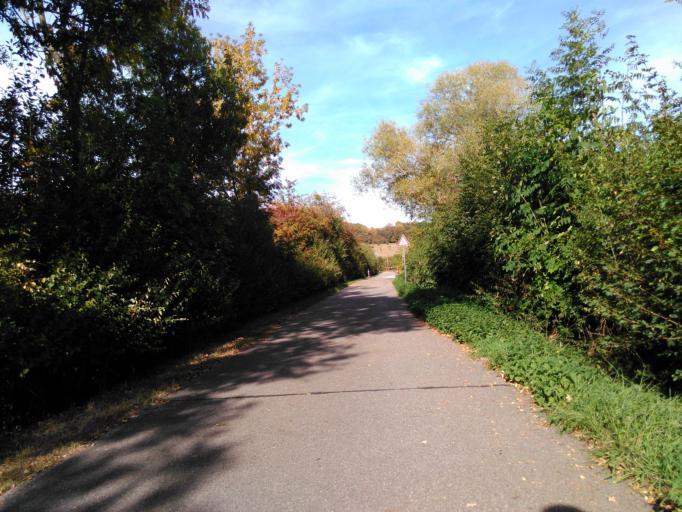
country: LU
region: Luxembourg
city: Hautcharage
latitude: 49.5766
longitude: 5.8962
